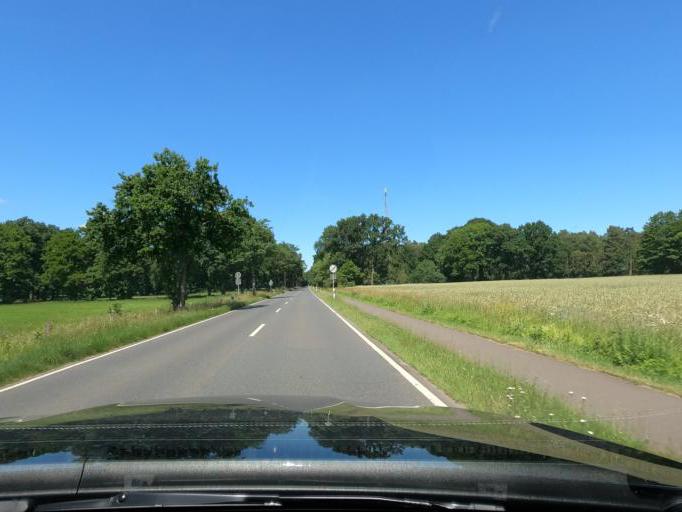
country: DE
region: Lower Saxony
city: Wienhausen
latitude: 52.5658
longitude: 10.1884
